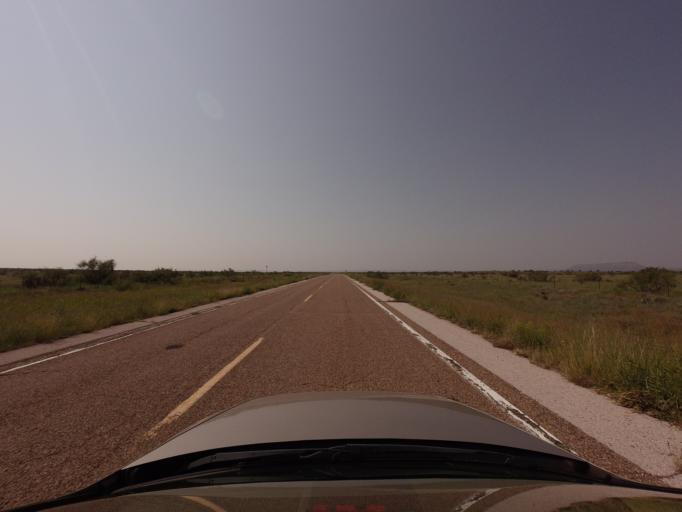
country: US
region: New Mexico
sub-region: Quay County
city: Tucumcari
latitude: 34.9841
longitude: -103.7490
